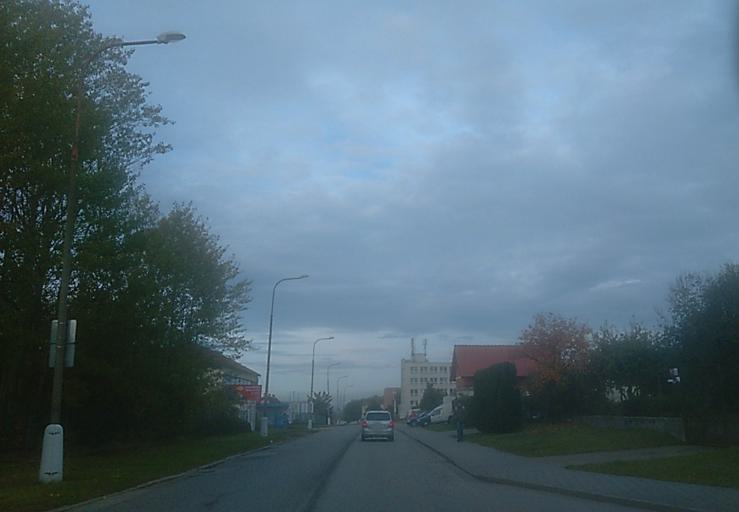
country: CZ
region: Jihocesky
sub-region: Okres Ceske Budejovice
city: Ceske Budejovice
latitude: 48.9751
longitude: 14.5093
